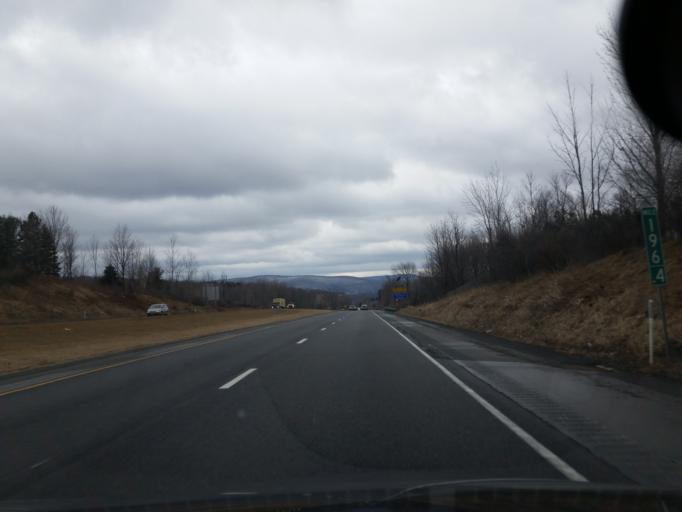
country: US
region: Pennsylvania
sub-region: Lackawanna County
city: Clarks Green
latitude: 41.5172
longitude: -75.6634
